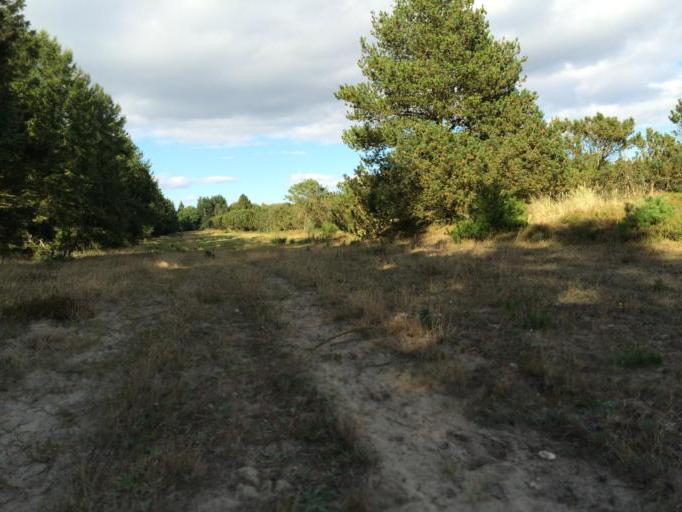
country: DK
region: Central Jutland
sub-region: Holstebro Kommune
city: Ulfborg
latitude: 56.2536
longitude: 8.4313
